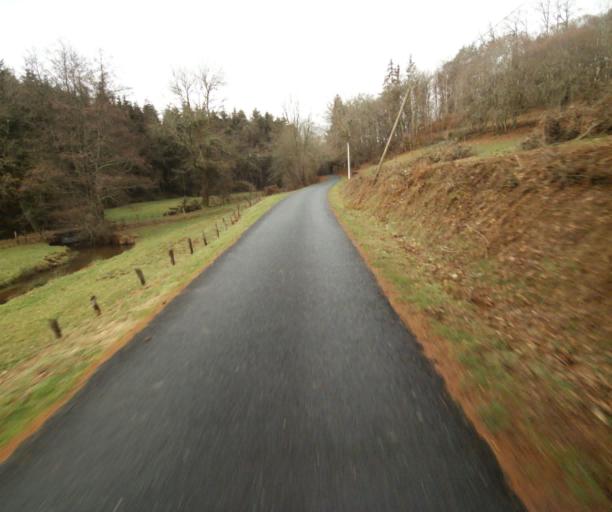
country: FR
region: Limousin
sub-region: Departement de la Correze
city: Saint-Mexant
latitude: 45.2999
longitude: 1.6368
